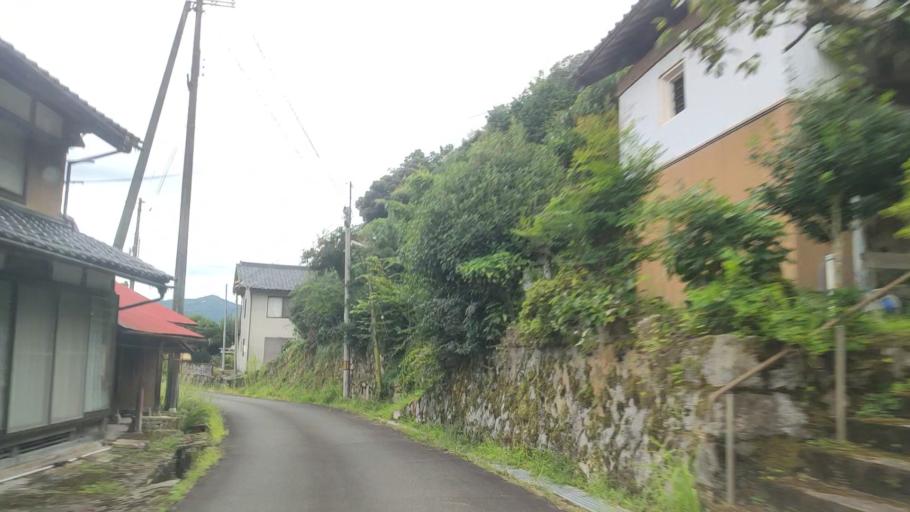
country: JP
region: Hyogo
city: Toyooka
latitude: 35.6005
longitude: 134.8798
